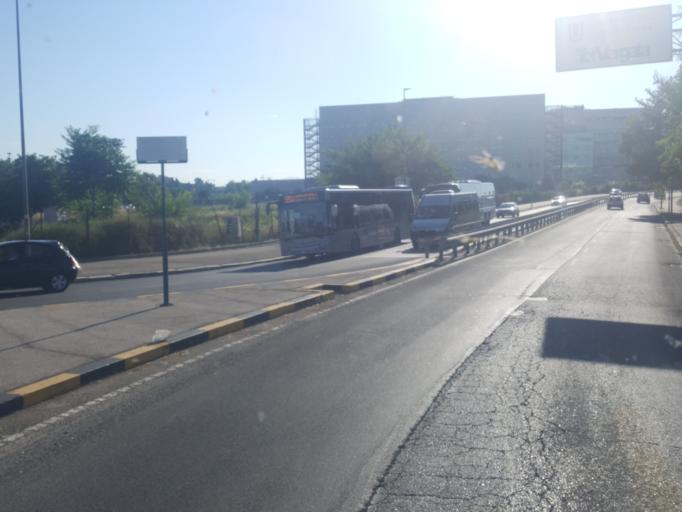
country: IT
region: Latium
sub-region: Citta metropolitana di Roma Capitale
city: Frascati
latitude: 41.8564
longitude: 12.6263
